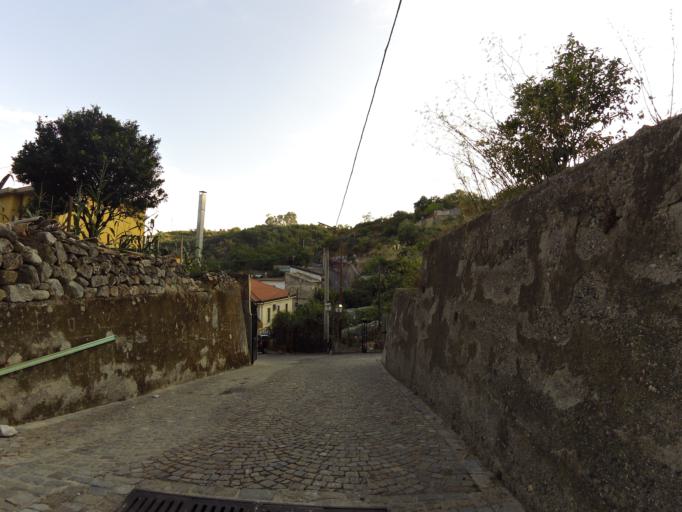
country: IT
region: Calabria
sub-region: Provincia di Reggio Calabria
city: Camini
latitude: 38.4327
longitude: 16.4814
